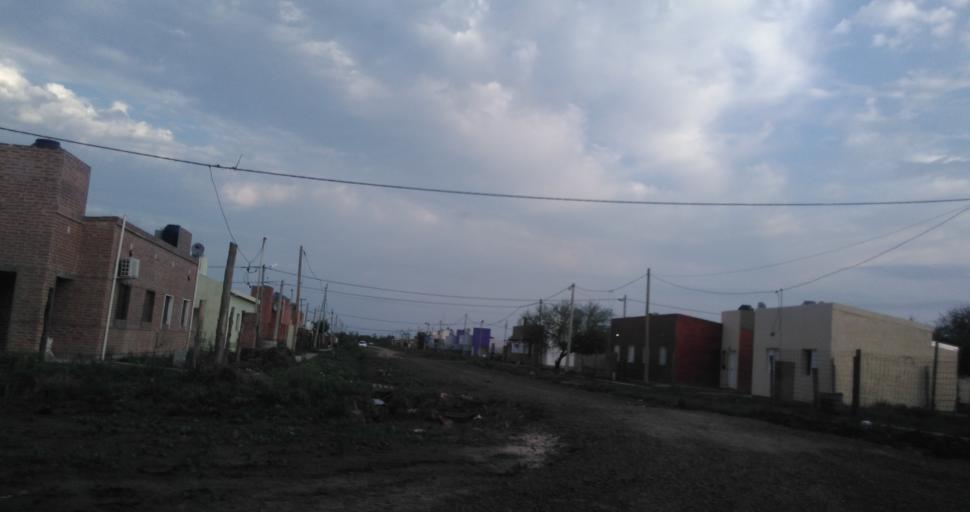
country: AR
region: Chaco
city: Resistencia
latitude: -27.4821
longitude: -59.0124
